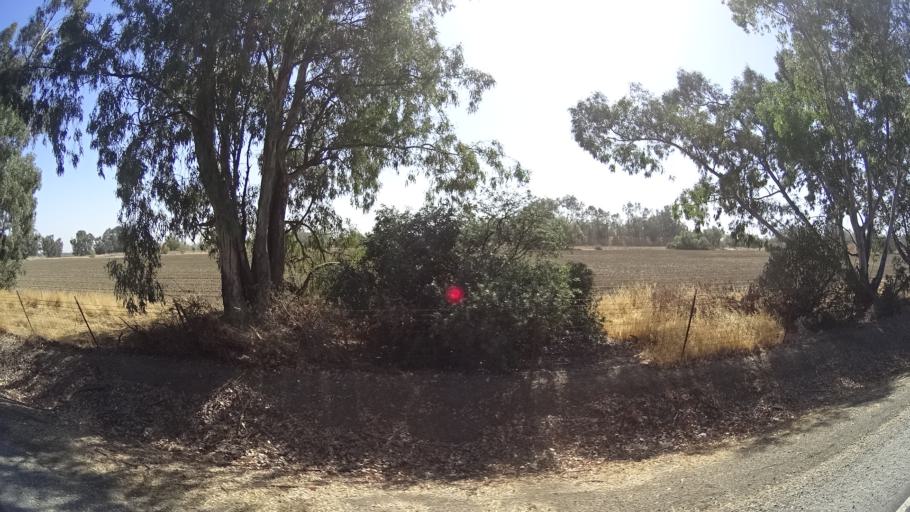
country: US
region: California
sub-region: Yolo County
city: Woodland
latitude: 38.5906
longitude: -121.8525
